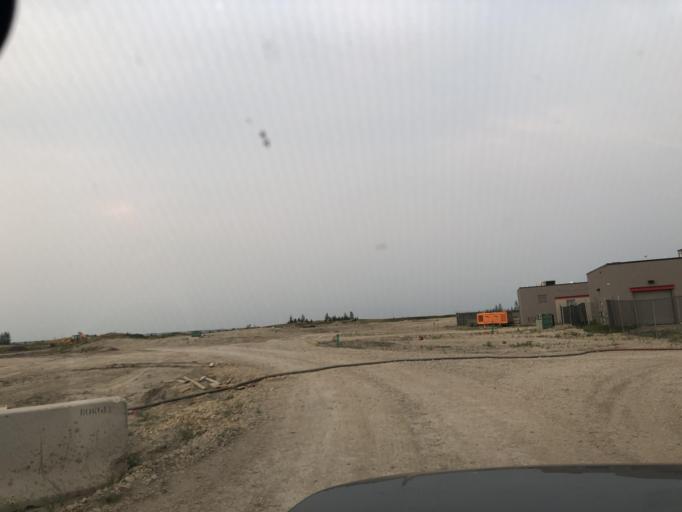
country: CA
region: Alberta
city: Cochrane
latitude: 51.1200
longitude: -114.3792
